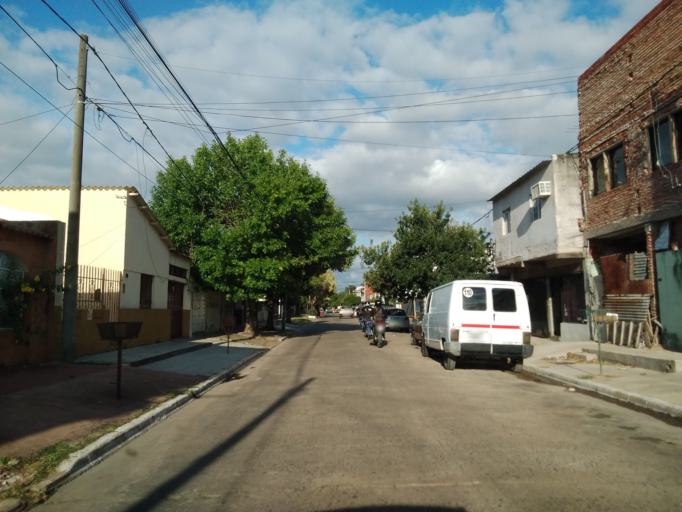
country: AR
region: Corrientes
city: Corrientes
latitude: -27.4655
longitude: -58.8217
